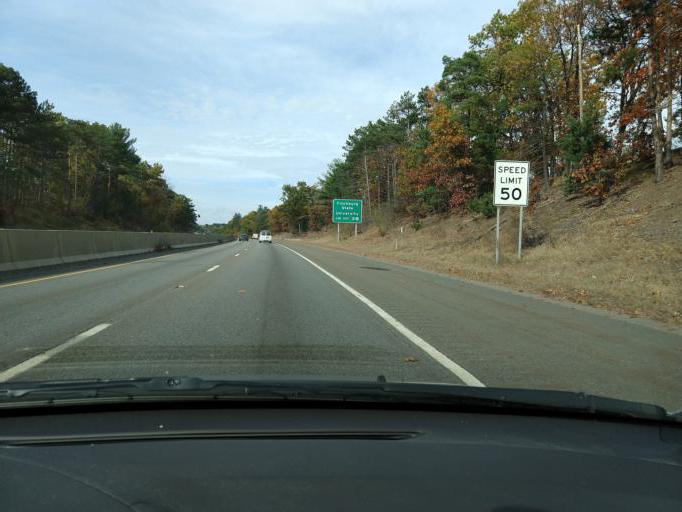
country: US
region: Massachusetts
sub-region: Worcester County
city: Leominster
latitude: 42.5435
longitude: -71.7529
